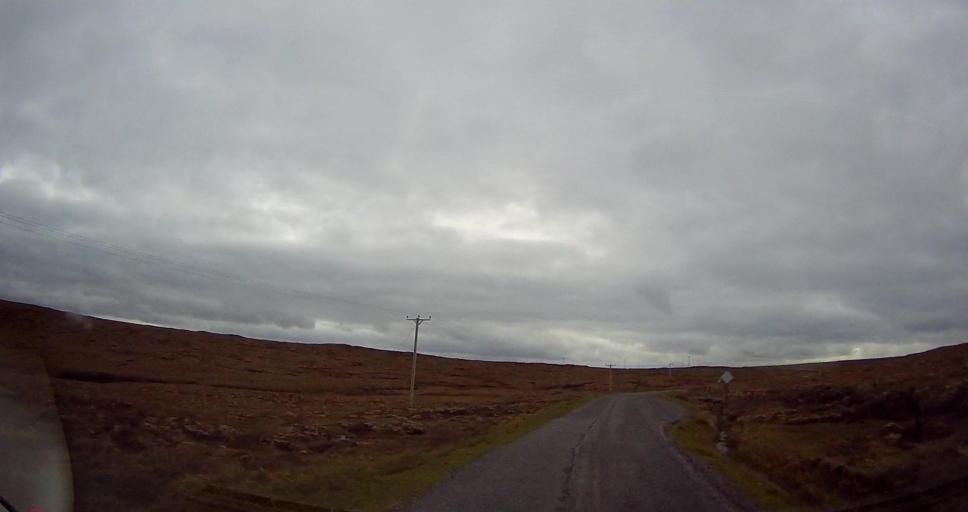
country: GB
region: Scotland
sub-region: Shetland Islands
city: Shetland
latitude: 60.5091
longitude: -1.1323
